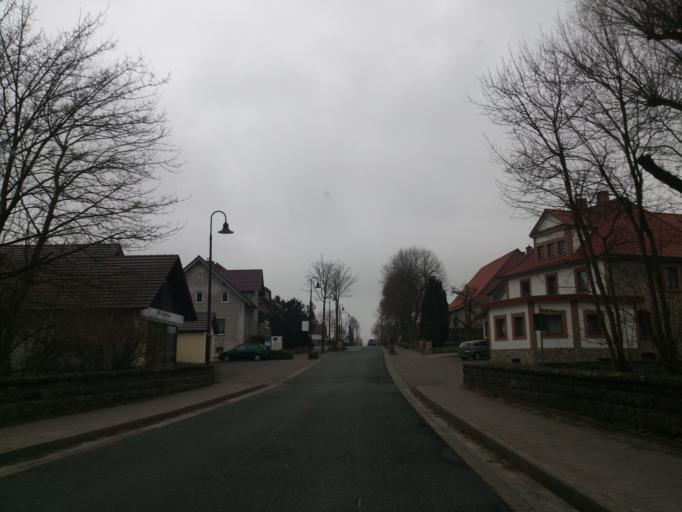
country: DE
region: North Rhine-Westphalia
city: Lichtenau
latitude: 51.6156
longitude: 8.8955
